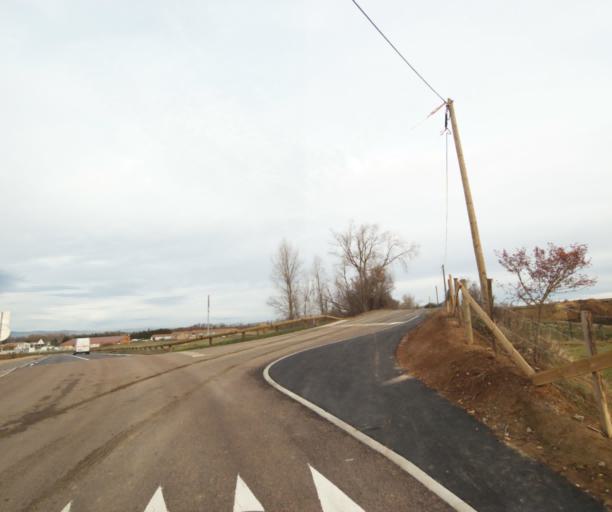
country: FR
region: Rhone-Alpes
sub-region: Departement de la Loire
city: Sury-le-Comtal
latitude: 45.5221
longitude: 4.1903
